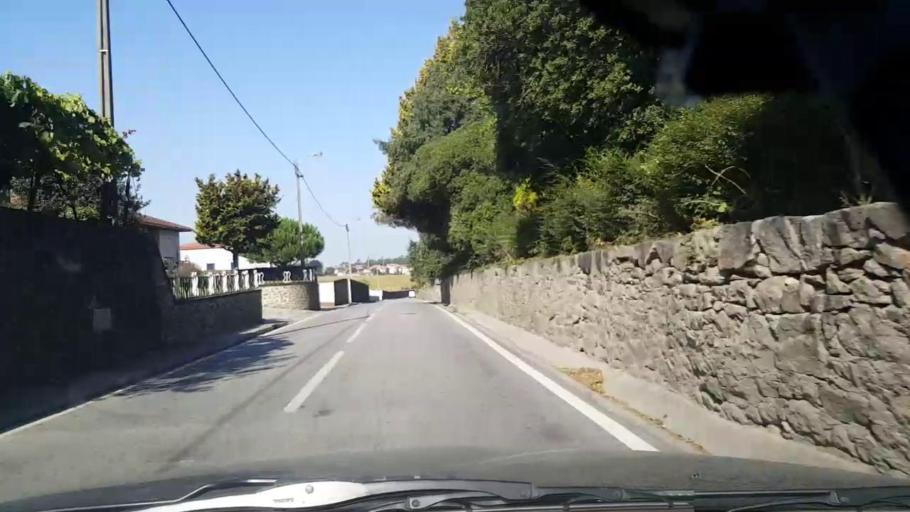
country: PT
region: Porto
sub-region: Vila do Conde
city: Arvore
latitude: 41.3762
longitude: -8.6735
